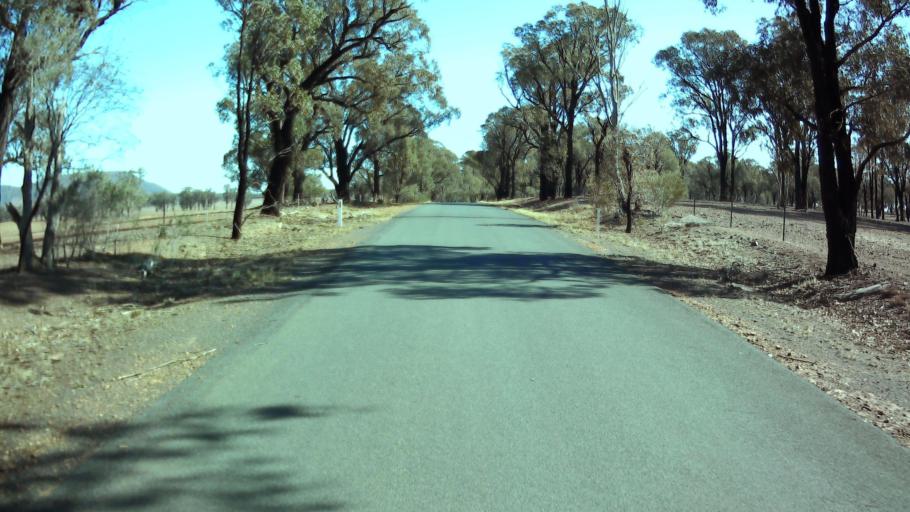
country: AU
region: New South Wales
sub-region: Weddin
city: Grenfell
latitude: -33.7871
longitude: 147.9581
